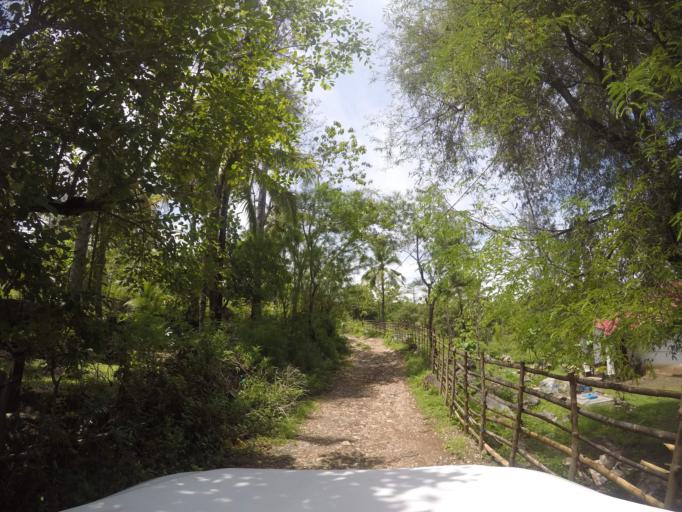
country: TL
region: Bobonaro
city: Maliana
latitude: -8.9988
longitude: 125.2249
